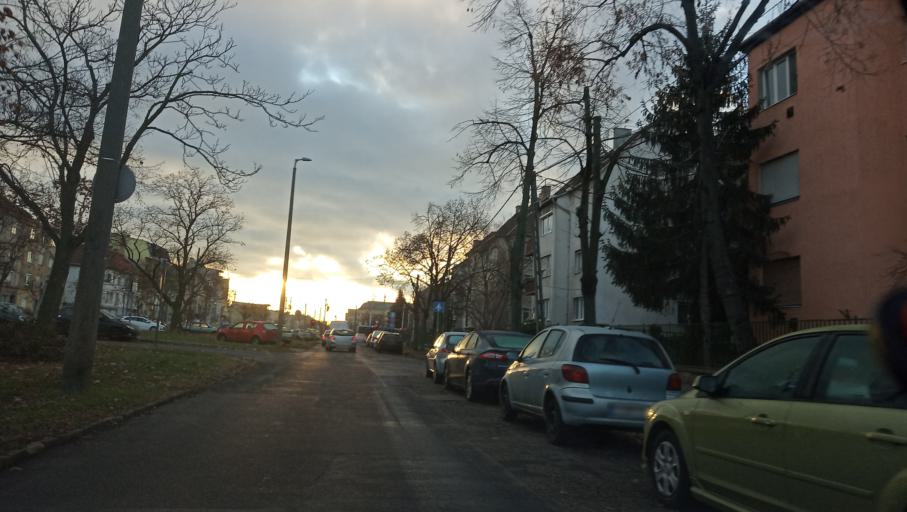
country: HU
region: Budapest
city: Budapest XIV. keruelet
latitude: 47.5226
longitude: 19.0993
